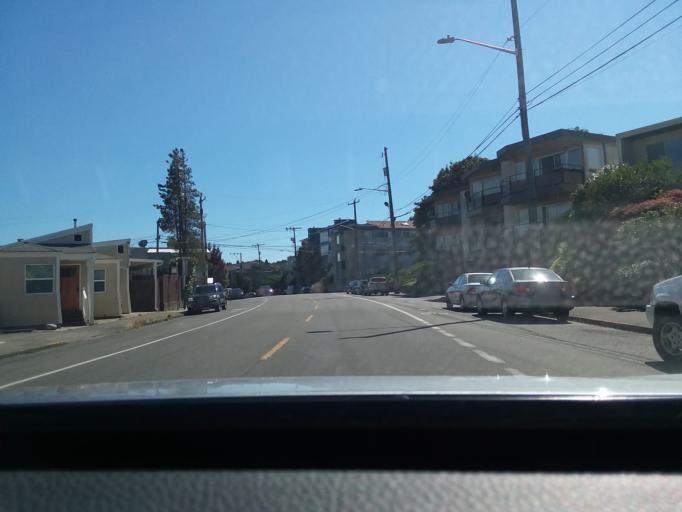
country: US
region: Washington
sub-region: King County
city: Shoreline
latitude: 47.6816
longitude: -122.3467
